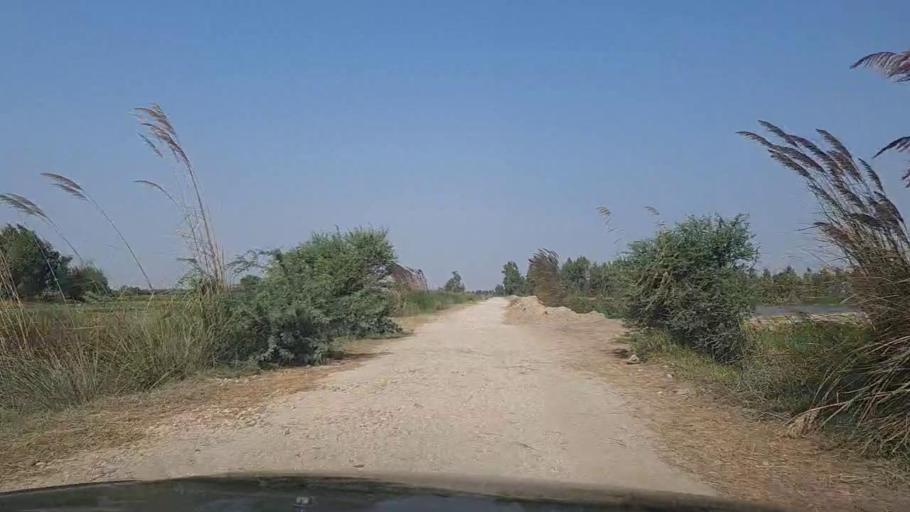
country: PK
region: Sindh
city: Thatta
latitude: 24.6206
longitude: 67.8153
